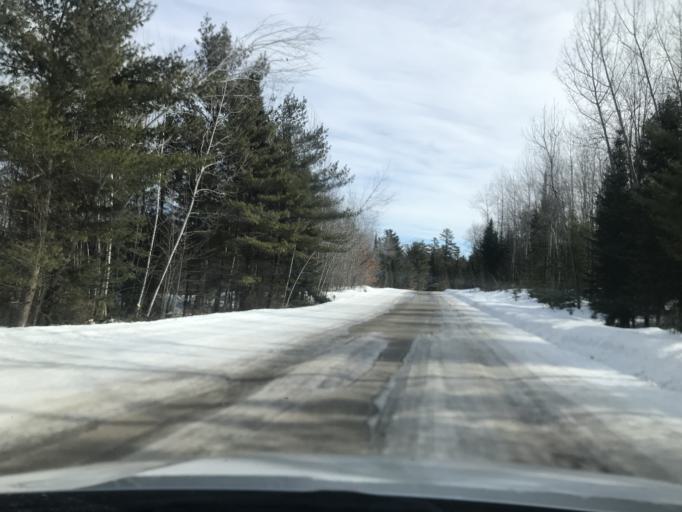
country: US
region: Wisconsin
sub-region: Menominee County
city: Legend Lake
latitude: 45.1100
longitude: -88.4370
